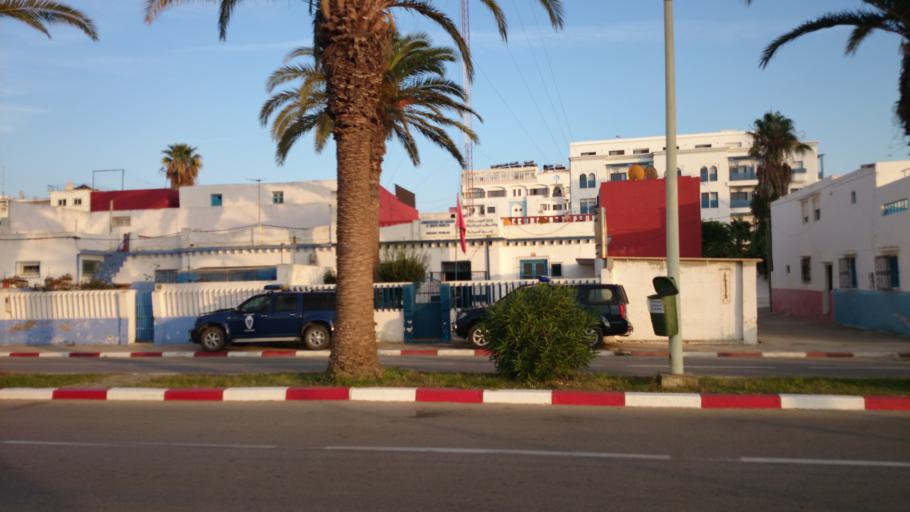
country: MA
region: Tanger-Tetouan
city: Asilah
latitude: 35.4690
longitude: -6.0336
